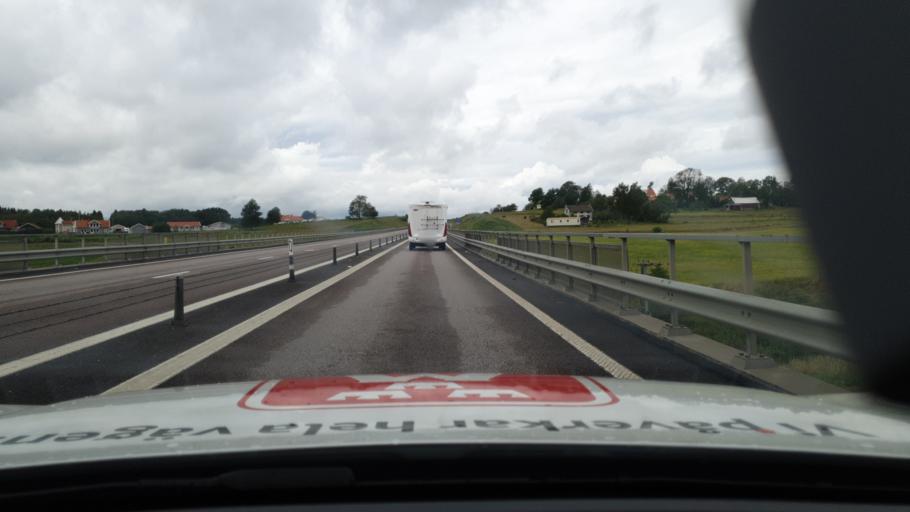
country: SE
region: Joenkoeping
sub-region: Jonkopings Kommun
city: Tenhult
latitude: 57.7368
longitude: 14.3001
